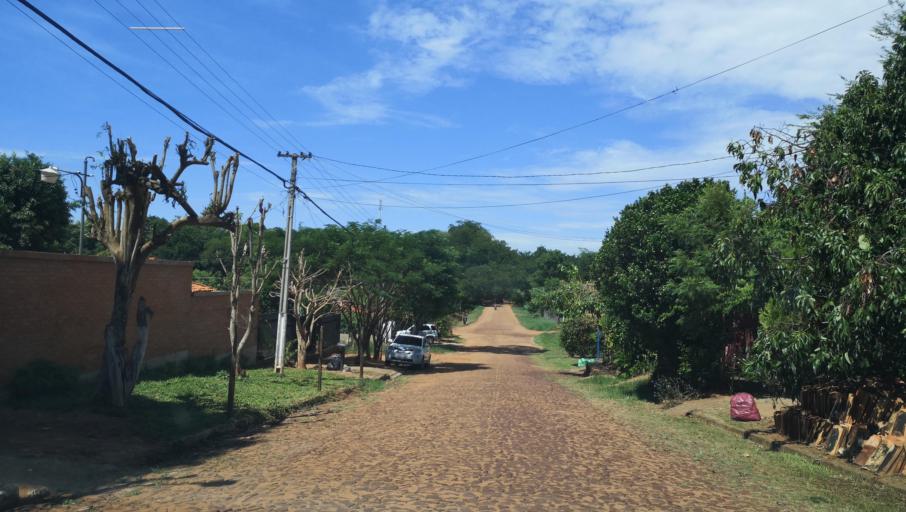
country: PY
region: Misiones
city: Santa Maria
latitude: -26.8820
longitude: -57.0265
